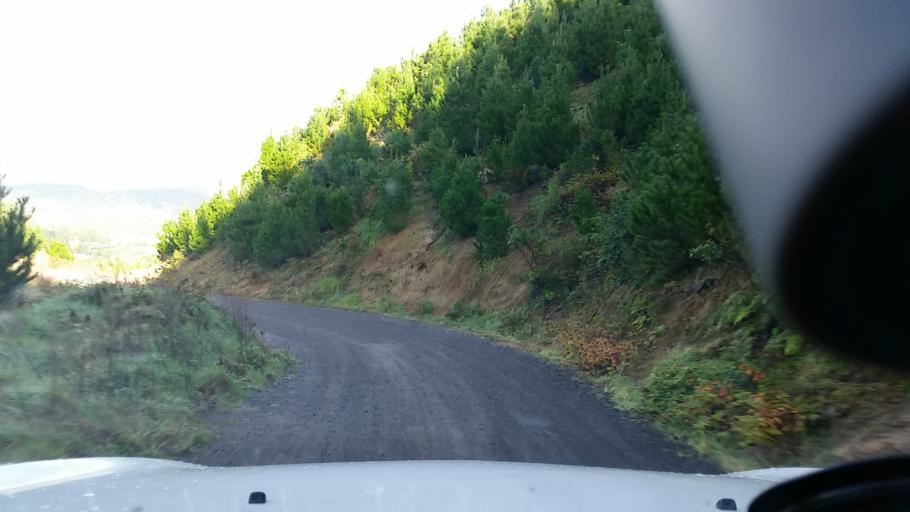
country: NZ
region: Bay of Plenty
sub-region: Kawerau District
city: Kawerau
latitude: -38.0299
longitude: 176.5563
